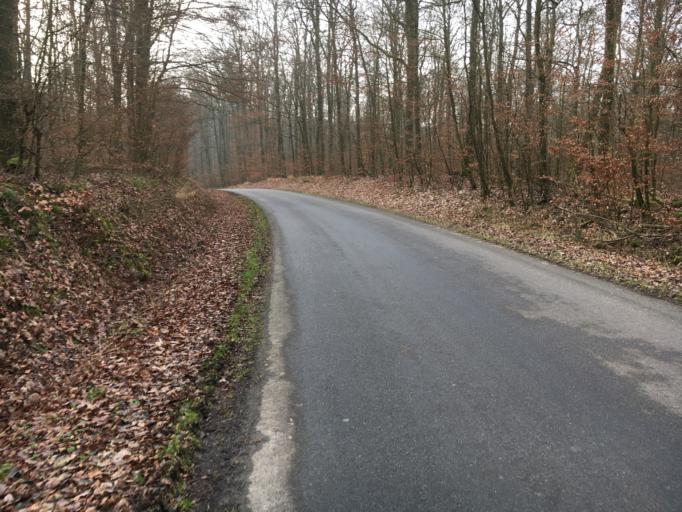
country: DE
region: Baden-Wuerttemberg
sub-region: Karlsruhe Region
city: Limbach
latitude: 49.4157
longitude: 9.2260
